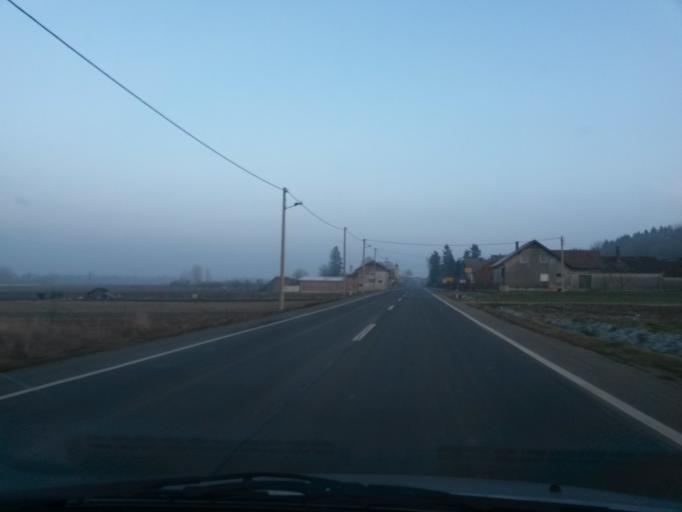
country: HR
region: Varazdinska
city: Ludbreg
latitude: 46.2328
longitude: 16.6553
